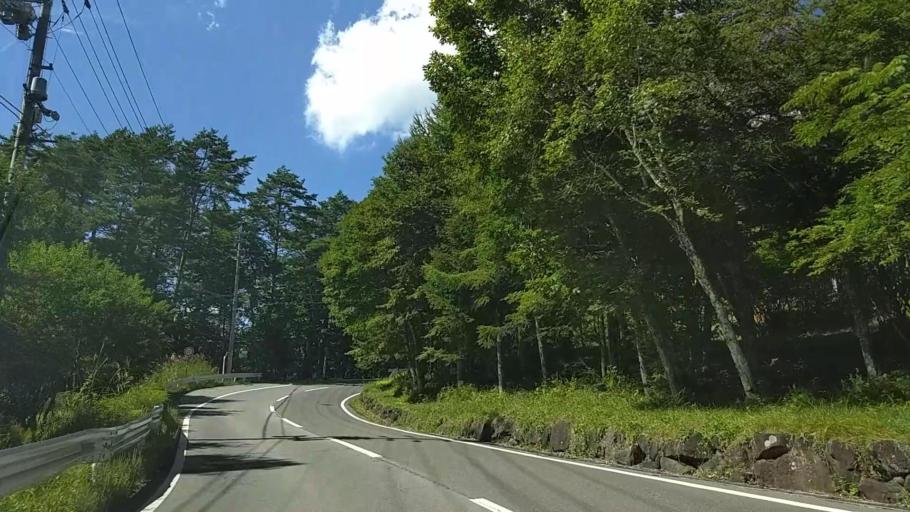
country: JP
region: Nagano
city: Chino
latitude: 36.0587
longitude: 138.2720
